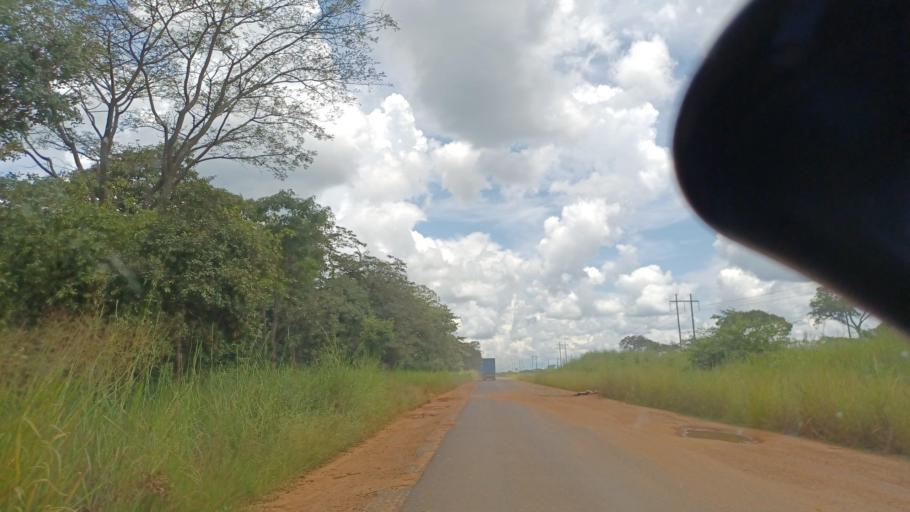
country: ZM
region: North-Western
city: Solwezi
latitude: -12.4350
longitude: 26.2108
